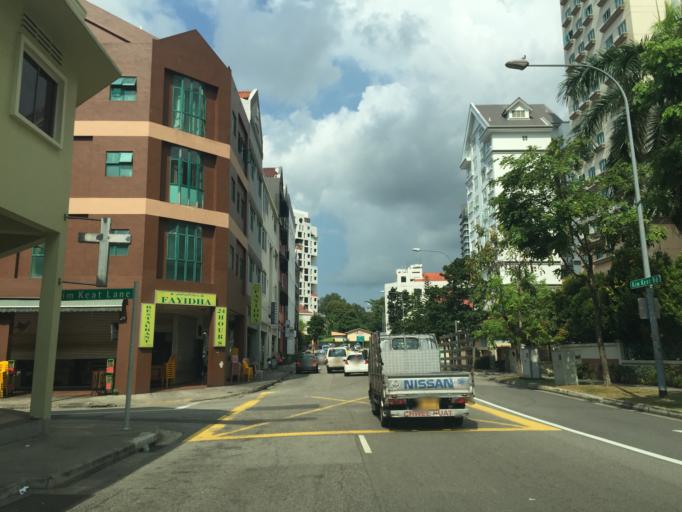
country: SG
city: Singapore
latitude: 1.3246
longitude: 103.8532
